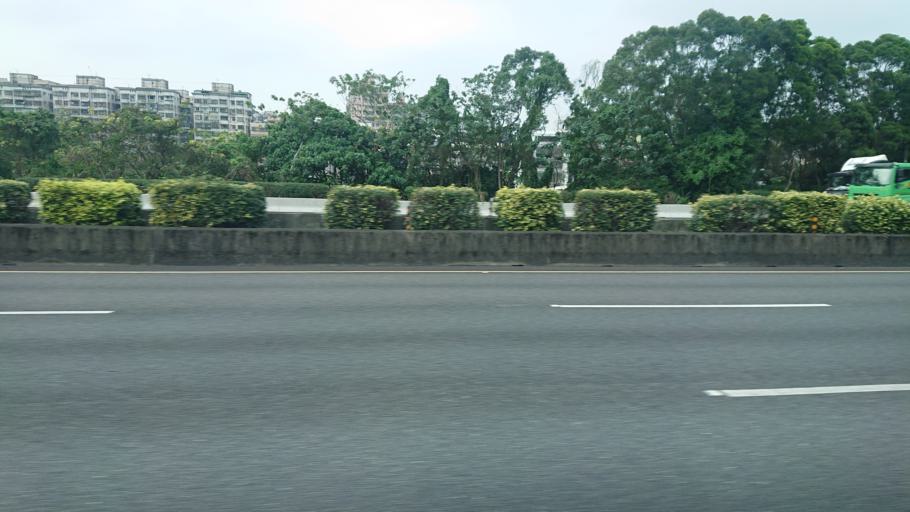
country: TW
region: Taipei
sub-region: Taipei
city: Banqiao
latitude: 24.9759
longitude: 121.4629
